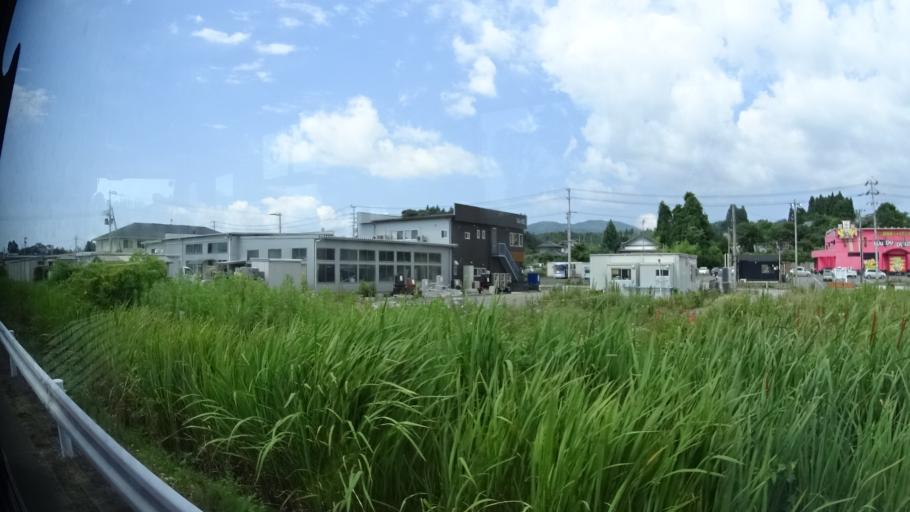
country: JP
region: Iwate
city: Ofunato
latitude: 38.8495
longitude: 141.5815
